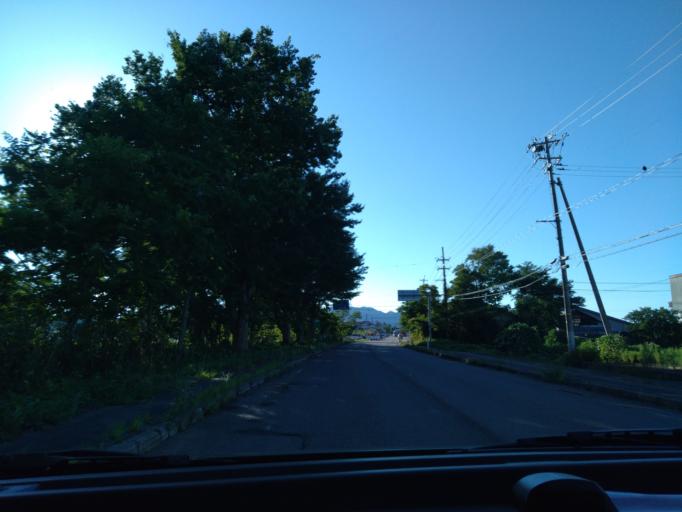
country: JP
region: Akita
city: Omagari
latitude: 39.4264
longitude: 140.4918
